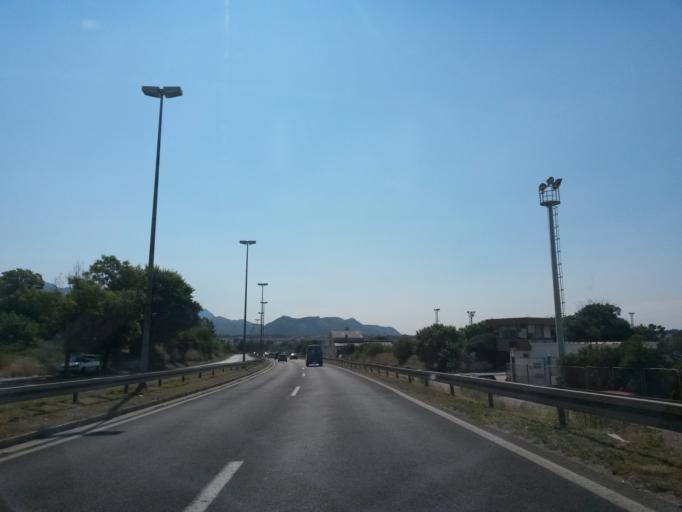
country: HR
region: Splitsko-Dalmatinska
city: Vranjic
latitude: 43.5380
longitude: 16.4726
